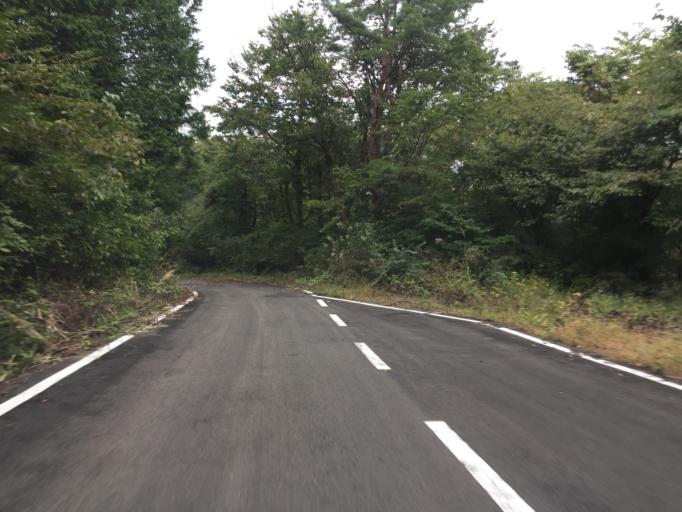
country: JP
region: Miyagi
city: Marumori
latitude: 37.9187
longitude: 140.7159
